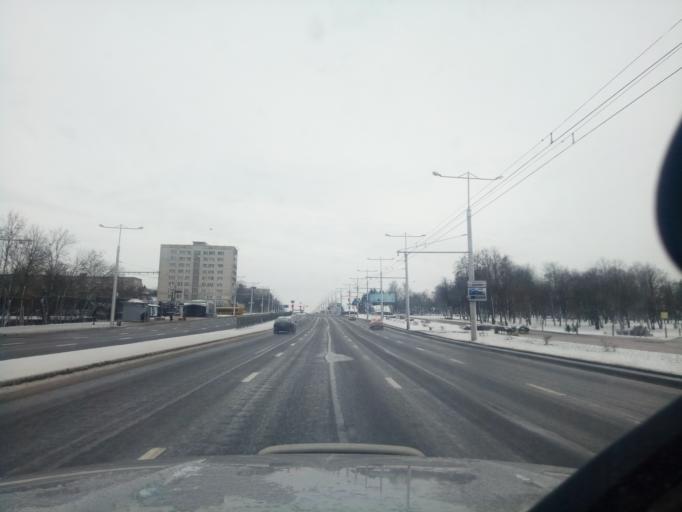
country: BY
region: Minsk
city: Hatava
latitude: 53.8509
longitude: 27.6333
